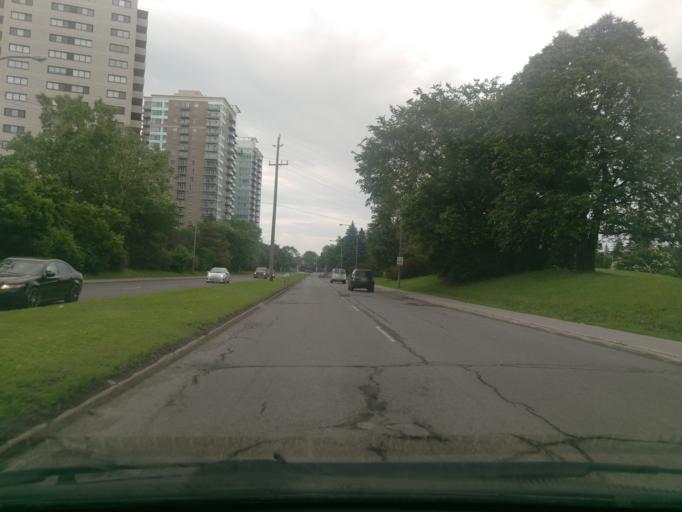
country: CA
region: Ontario
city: Ottawa
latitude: 45.4377
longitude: -75.6753
